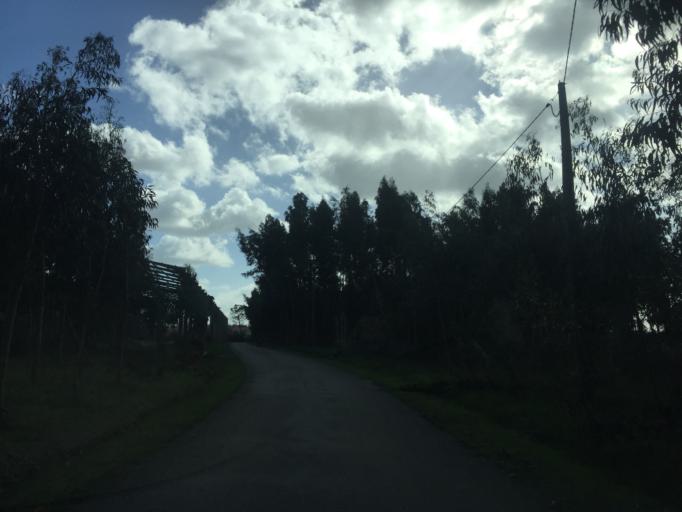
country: PT
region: Coimbra
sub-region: Figueira da Foz
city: Lavos
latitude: 40.0188
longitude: -8.8219
